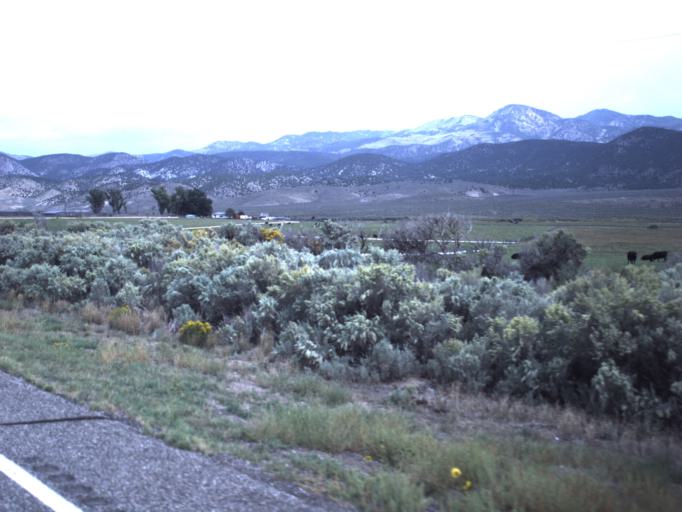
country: US
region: Utah
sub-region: Garfield County
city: Panguitch
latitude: 38.0043
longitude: -112.3814
